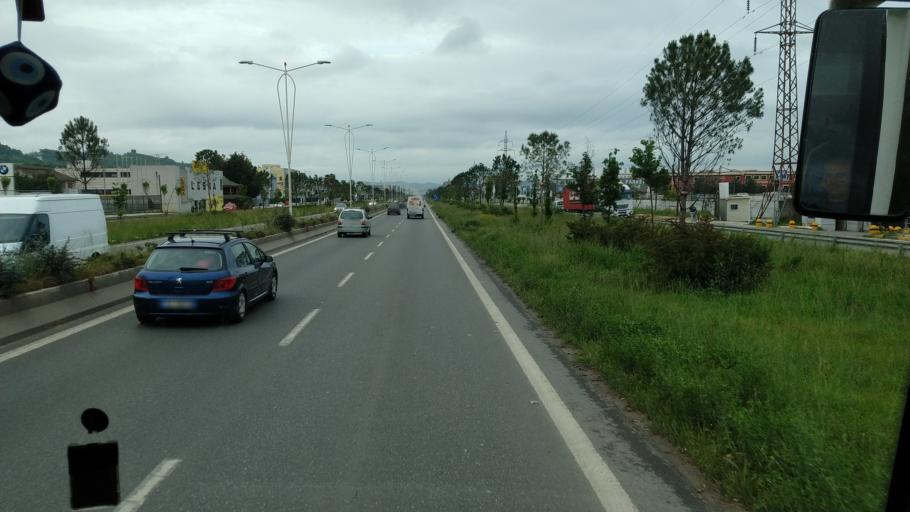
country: AL
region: Tirane
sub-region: Rrethi i Tiranes
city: Kamez
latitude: 41.3483
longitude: 19.7608
